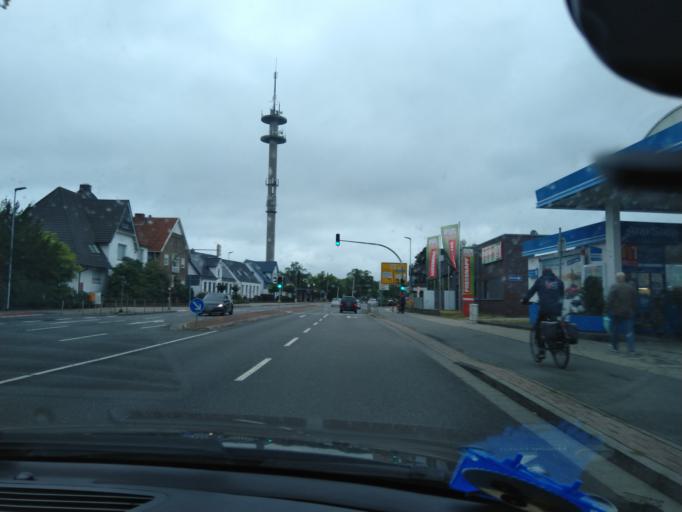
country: DE
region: Lower Saxony
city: Nordhorn
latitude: 52.4293
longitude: 7.0623
